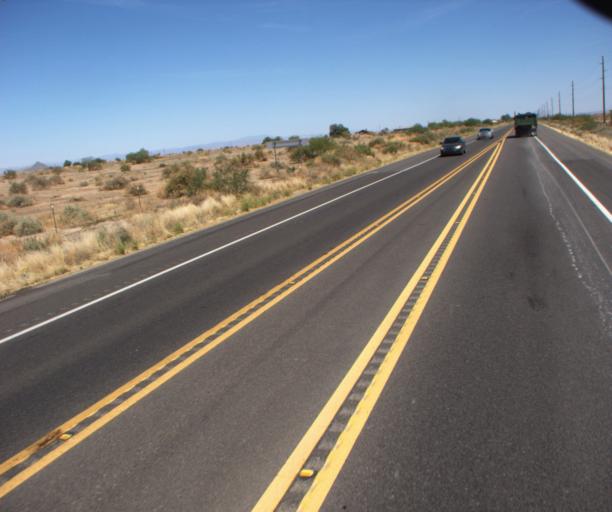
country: US
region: Arizona
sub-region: Pinal County
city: Blackwater
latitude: 33.0025
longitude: -111.5919
